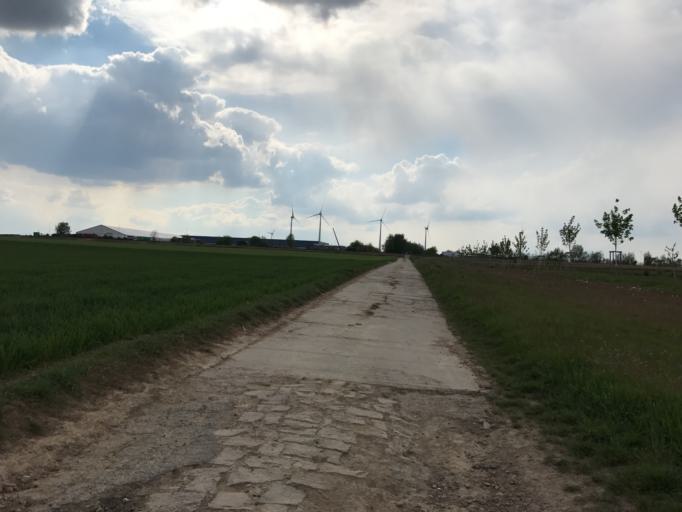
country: DE
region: Rheinland-Pfalz
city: Gau-Bischofsheim
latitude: 49.9434
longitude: 8.2620
